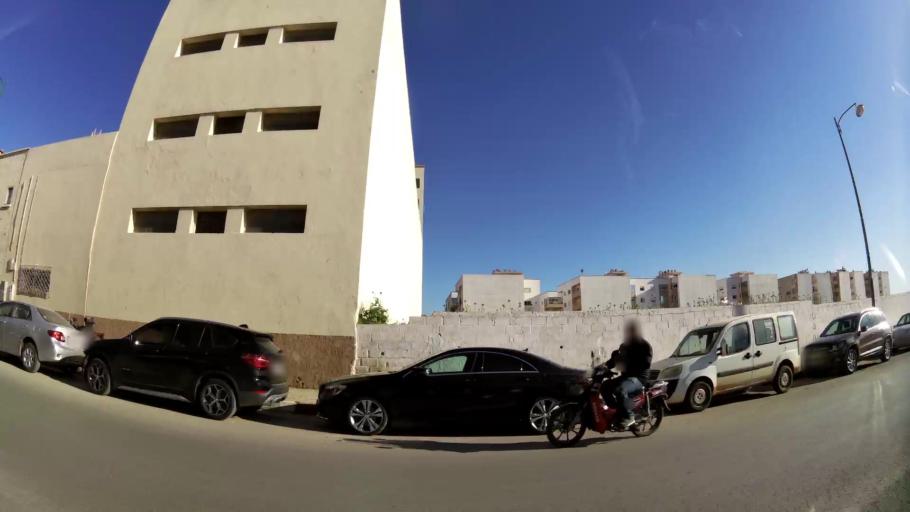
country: MA
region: Meknes-Tafilalet
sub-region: Meknes
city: Meknes
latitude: 33.8930
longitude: -5.5238
